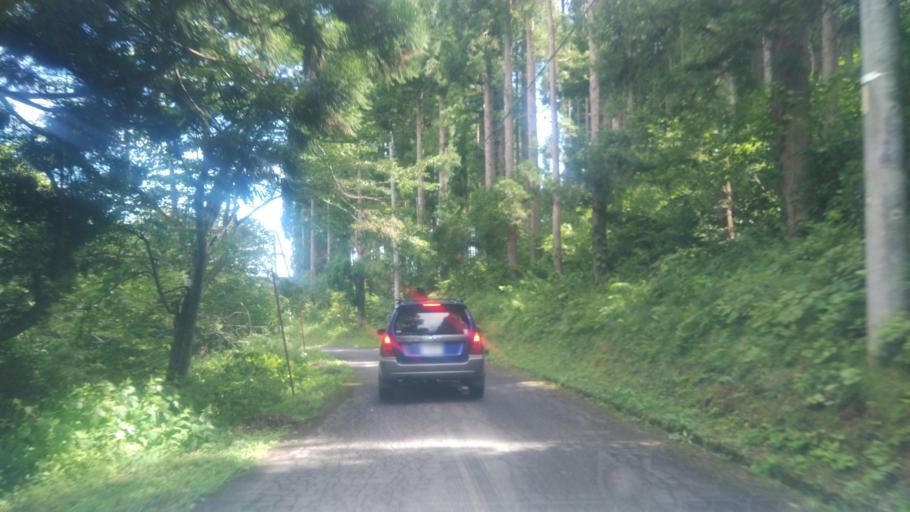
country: JP
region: Niigata
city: Arai
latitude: 36.8409
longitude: 138.1709
